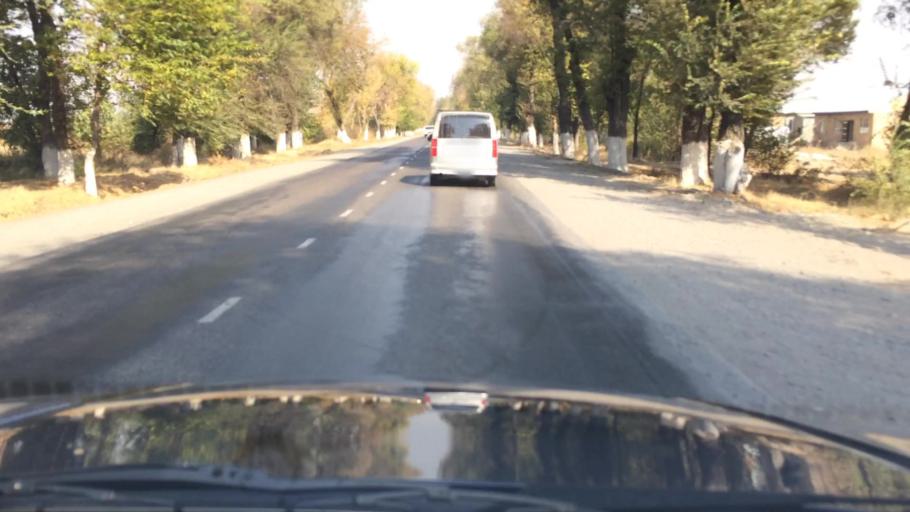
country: KG
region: Chuy
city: Lebedinovka
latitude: 42.9221
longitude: 74.6898
